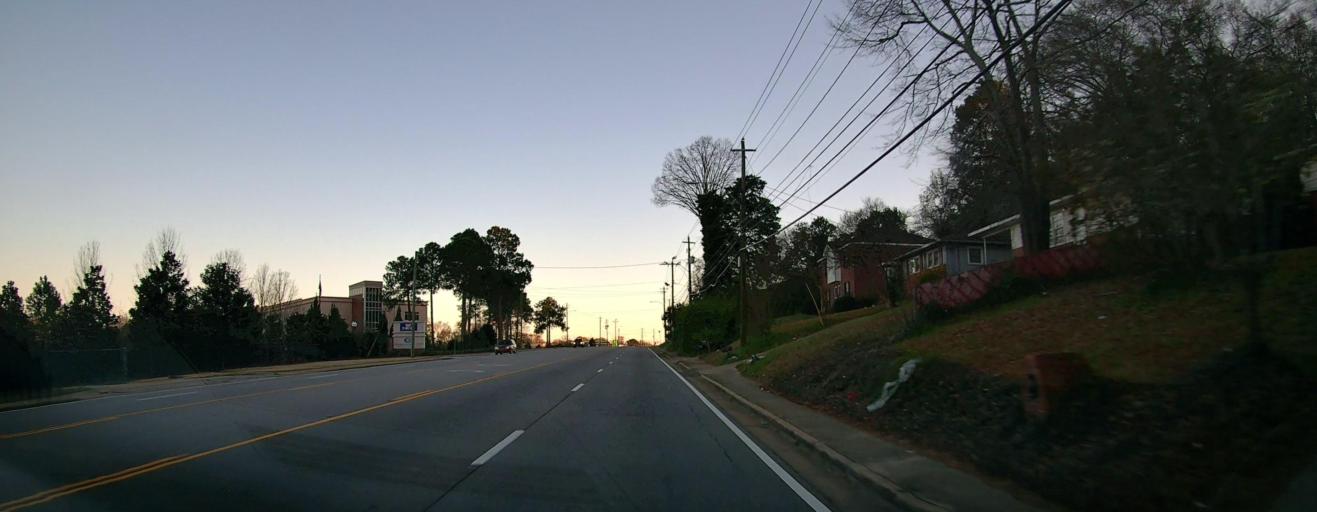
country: US
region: Alabama
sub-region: Russell County
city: Phenix City
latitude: 32.5103
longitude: -84.9799
